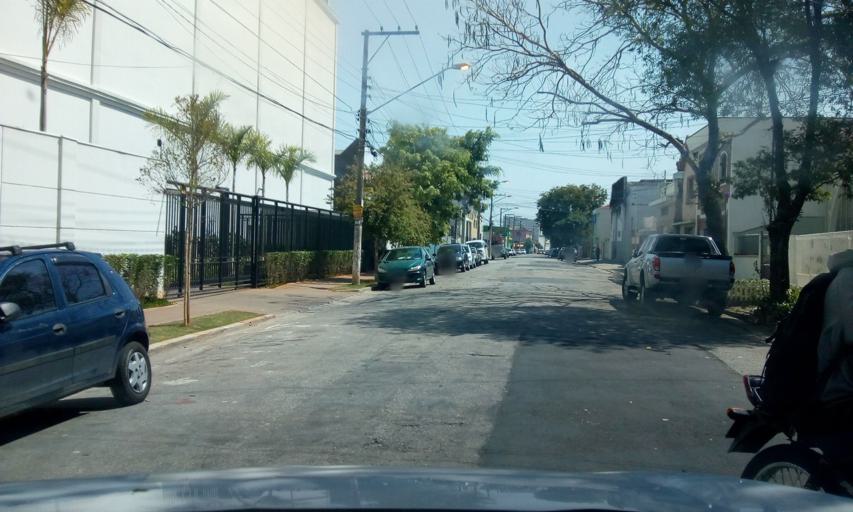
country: BR
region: Sao Paulo
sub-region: Osasco
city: Osasco
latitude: -23.5167
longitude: -46.7186
